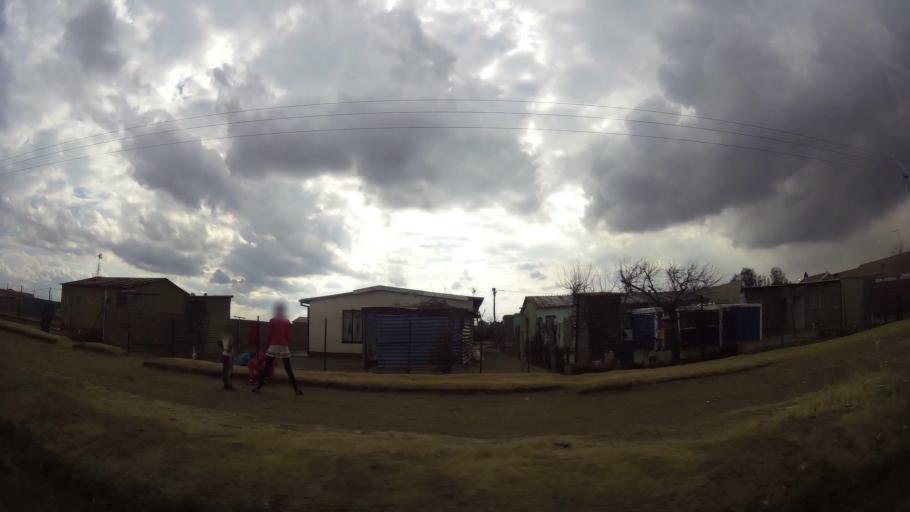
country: ZA
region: Orange Free State
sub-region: Fezile Dabi District Municipality
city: Sasolburg
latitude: -26.8548
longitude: 27.8534
